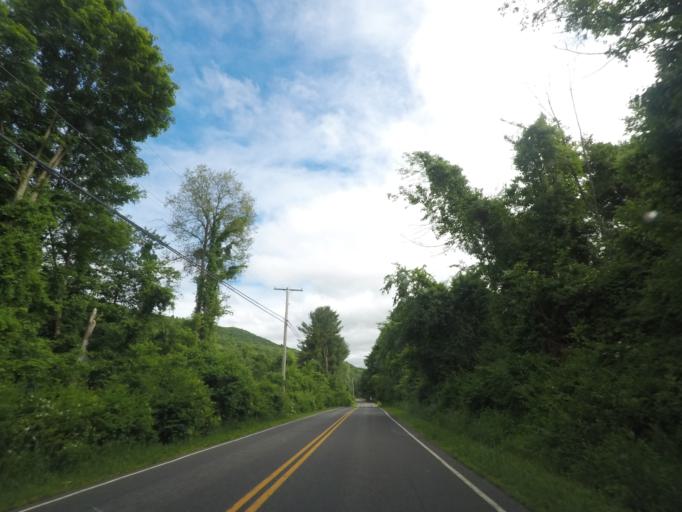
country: US
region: New York
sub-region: Dutchess County
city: Pine Plains
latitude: 42.0125
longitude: -73.5091
